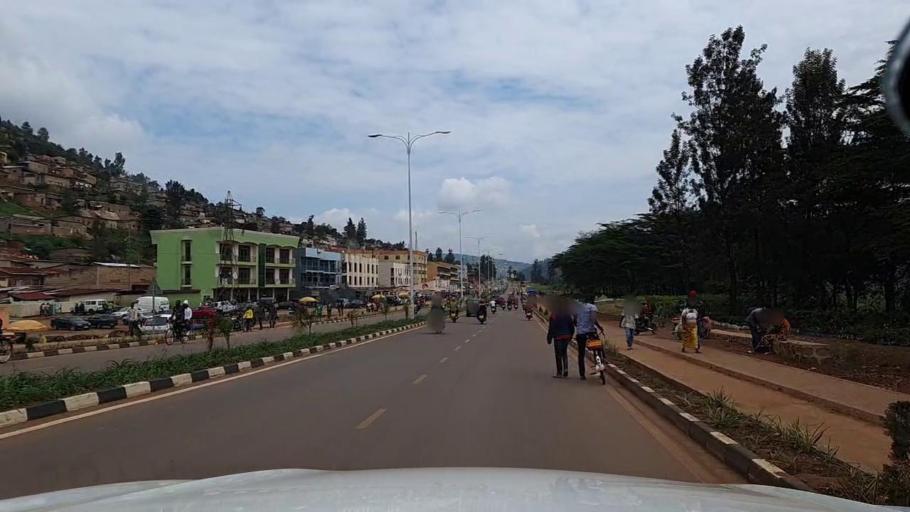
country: RW
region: Kigali
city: Kigali
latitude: -1.9386
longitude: 30.0441
